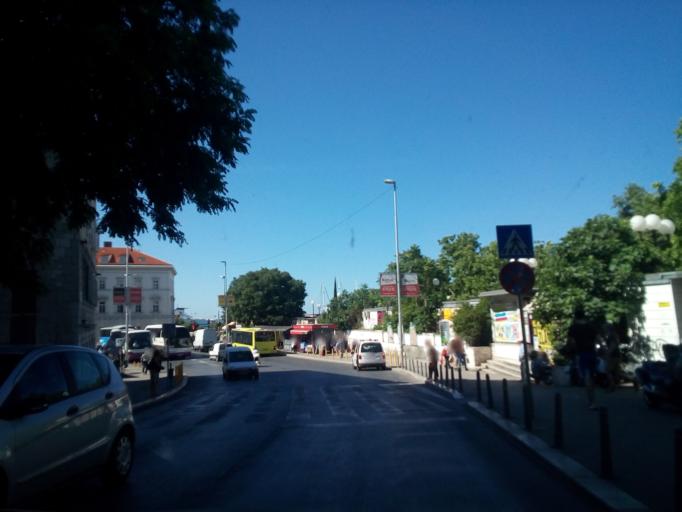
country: HR
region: Splitsko-Dalmatinska
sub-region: Grad Split
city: Split
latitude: 43.5082
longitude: 16.4426
